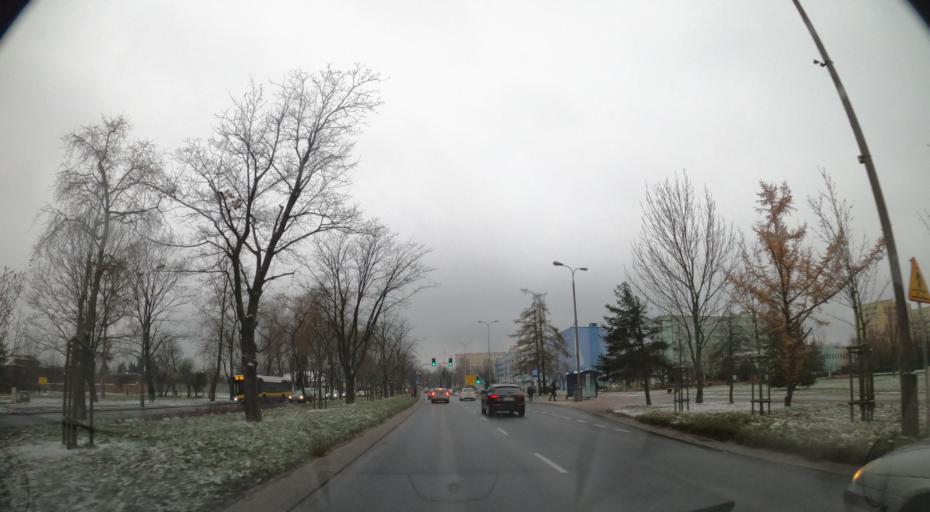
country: PL
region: Masovian Voivodeship
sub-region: Plock
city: Plock
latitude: 52.5503
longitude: 19.6877
